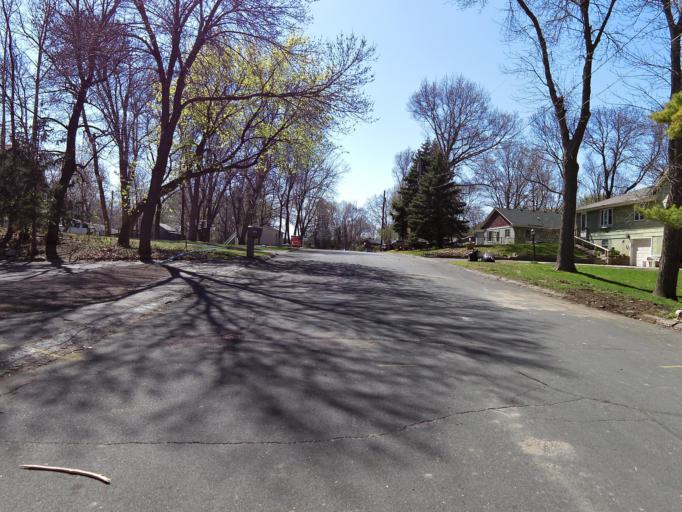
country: US
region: Minnesota
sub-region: Scott County
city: Prior Lake
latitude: 44.7217
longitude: -93.4356
